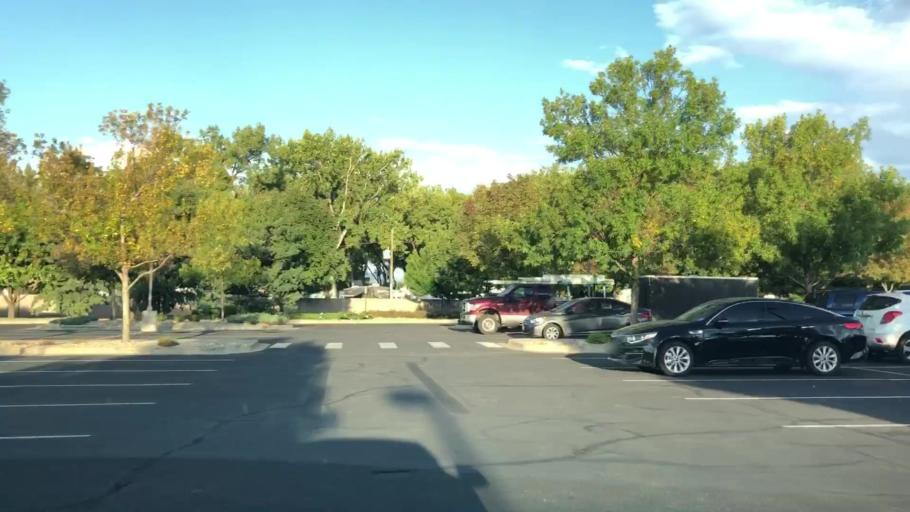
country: US
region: Colorado
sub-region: Larimer County
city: Loveland
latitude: 40.4086
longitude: -105.0105
